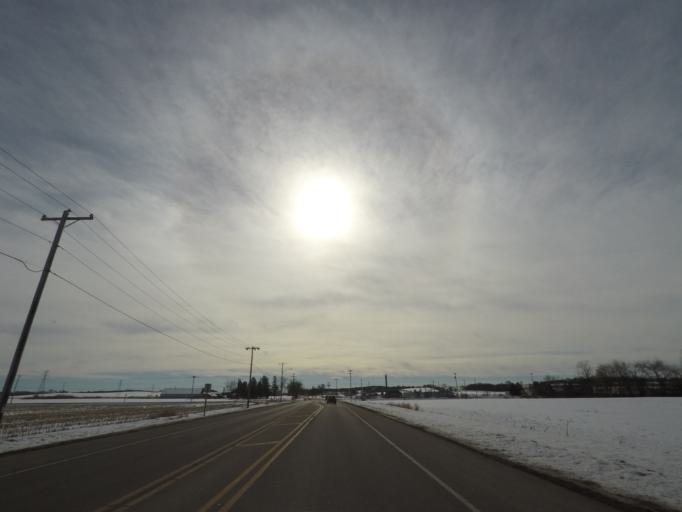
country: US
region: Wisconsin
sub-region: Dane County
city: Fitchburg
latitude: 43.0025
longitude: -89.4589
